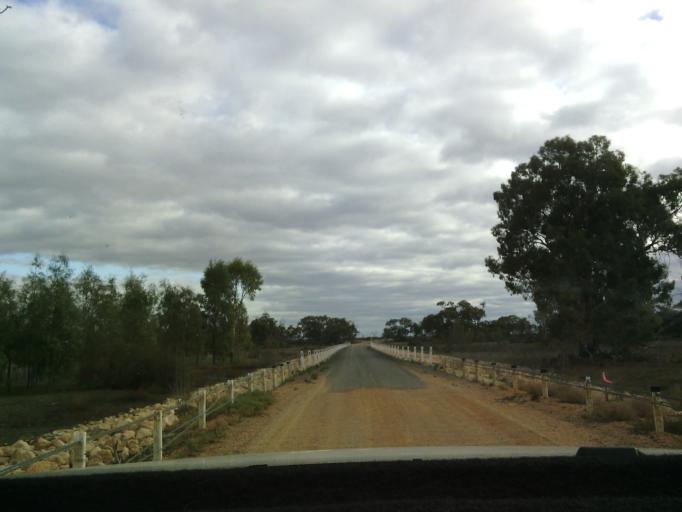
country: AU
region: South Australia
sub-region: Renmark Paringa
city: Renmark
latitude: -34.1677
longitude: 141.1844
